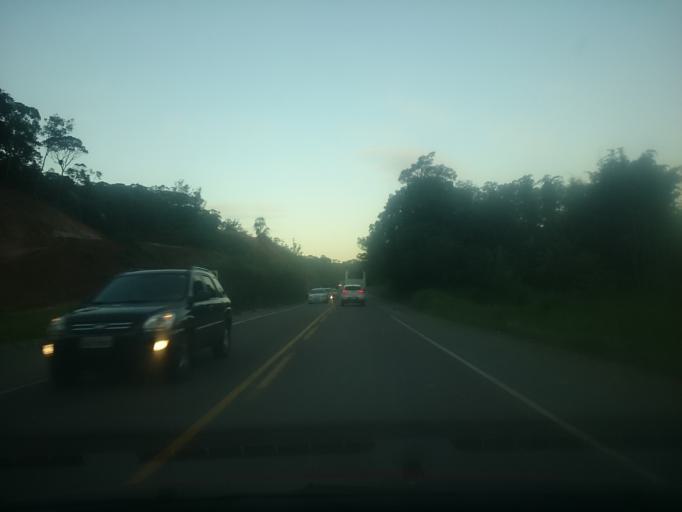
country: BR
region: Santa Catarina
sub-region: Itajai
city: Itajai
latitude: -26.8397
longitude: -48.7875
